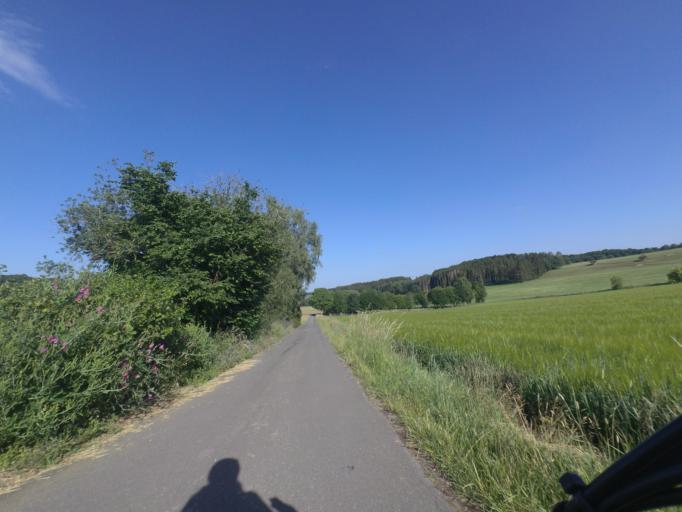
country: DE
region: Rheinland-Pfalz
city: Esch
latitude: 50.3656
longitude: 6.6143
